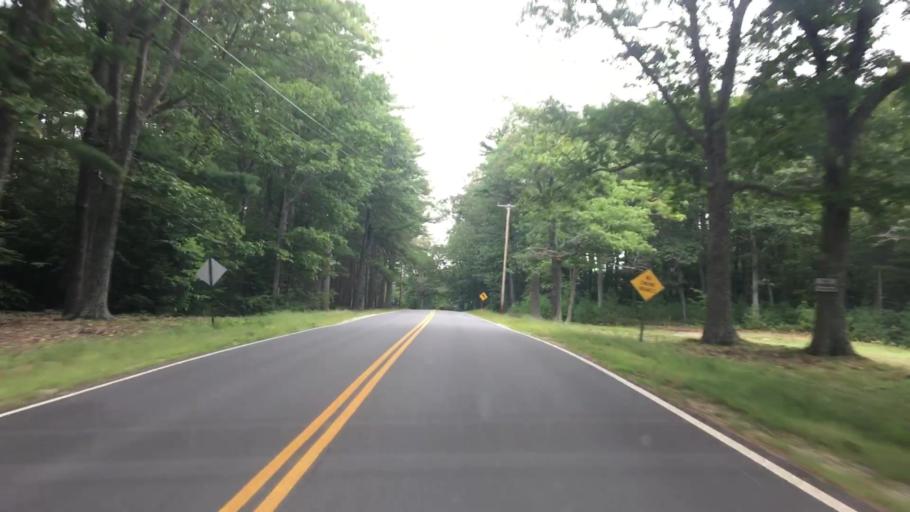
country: US
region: Maine
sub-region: Cumberland County
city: New Gloucester
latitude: 43.9029
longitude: -70.2520
